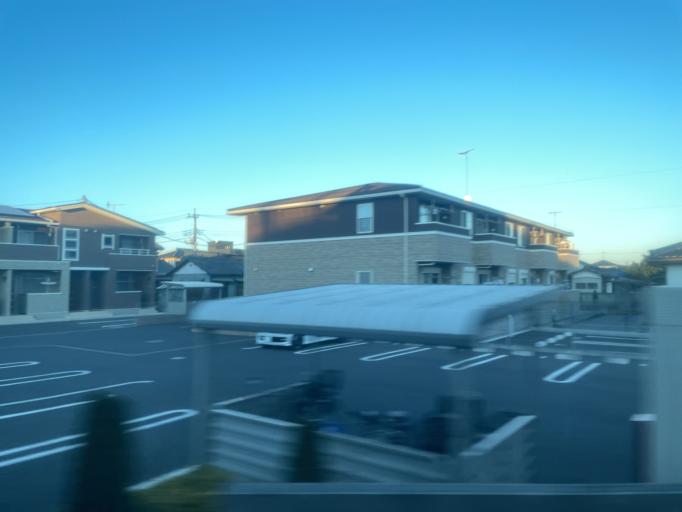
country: JP
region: Saitama
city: Honjo
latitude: 36.2299
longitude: 139.1988
